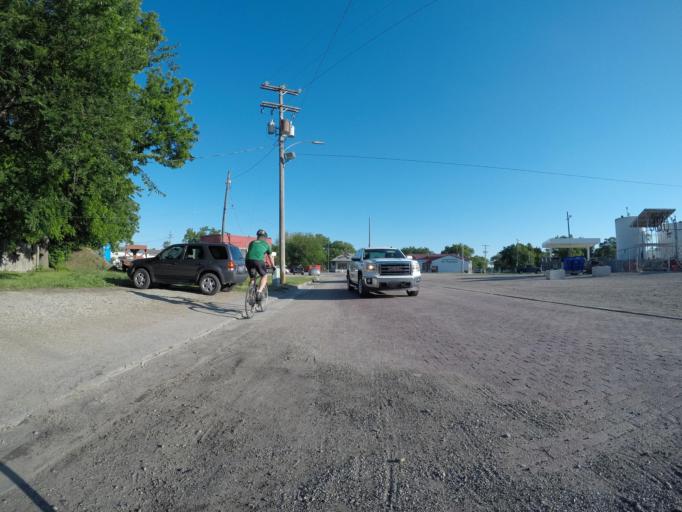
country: US
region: Kansas
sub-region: Morris County
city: Council Grove
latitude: 38.6610
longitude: -96.4796
